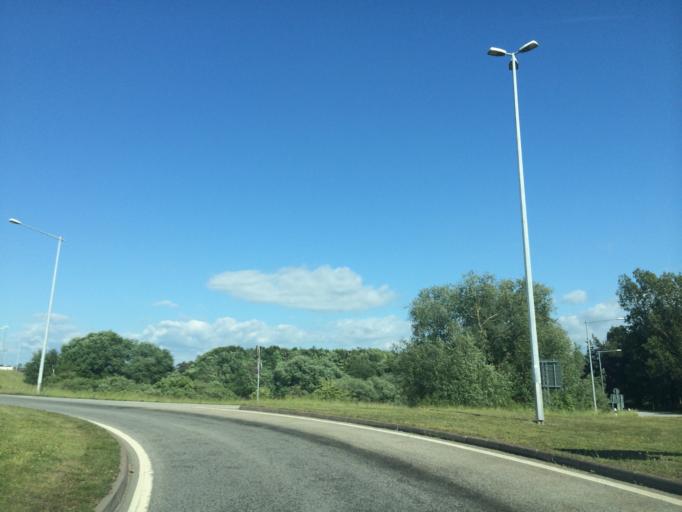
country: SE
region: Skane
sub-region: Kavlinge Kommun
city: Hofterup
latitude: 55.7652
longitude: 12.9850
